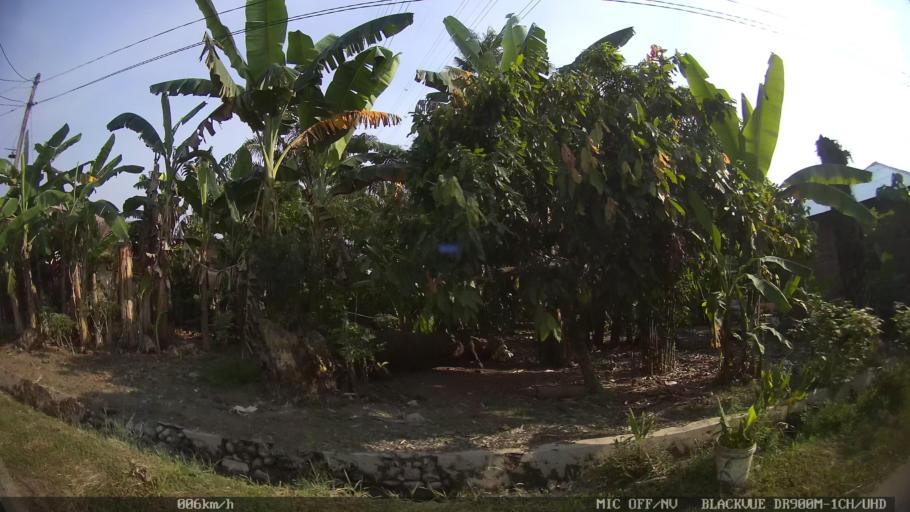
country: ID
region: North Sumatra
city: Binjai
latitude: 3.6209
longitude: 98.5184
